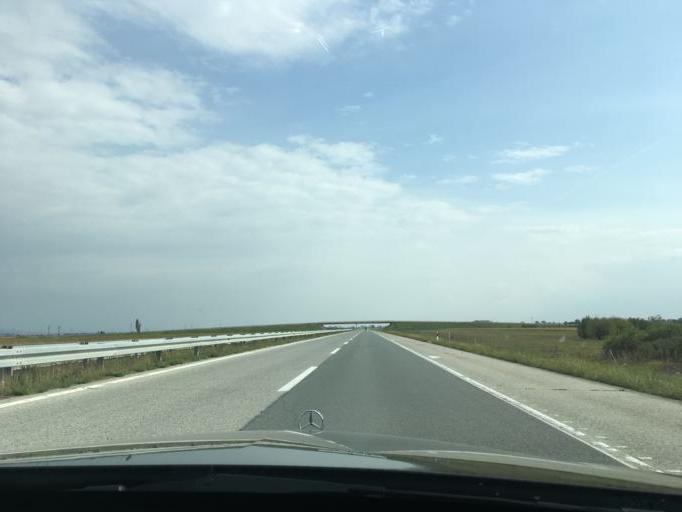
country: RS
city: Macvanska Mitrovica
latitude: 45.0179
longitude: 19.5378
